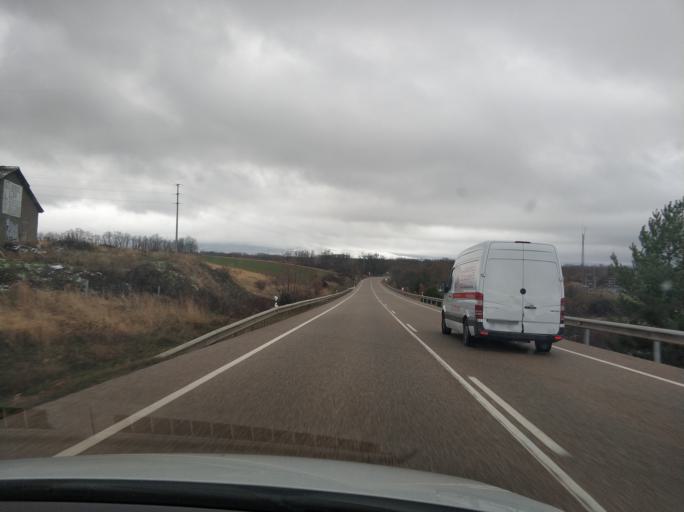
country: ES
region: Castille and Leon
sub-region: Provincia de Segovia
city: Riaza
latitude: 41.2763
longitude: -3.4936
